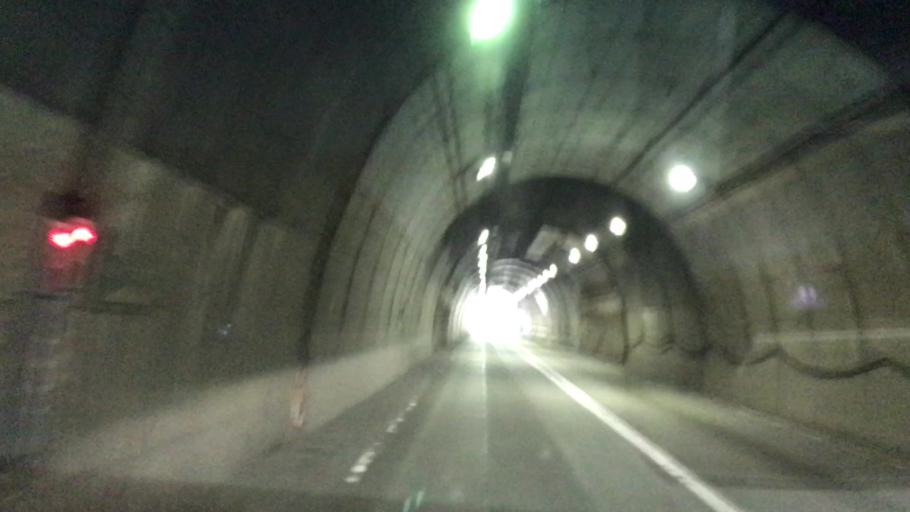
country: JP
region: Hokkaido
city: Yoichi
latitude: 43.0522
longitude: 140.6824
